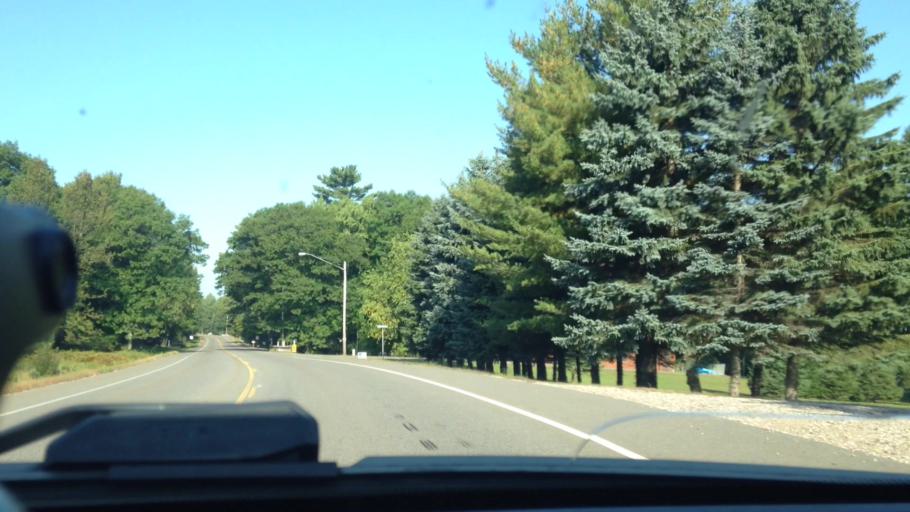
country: US
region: Michigan
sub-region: Dickinson County
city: Quinnesec
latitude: 45.8289
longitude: -87.9945
